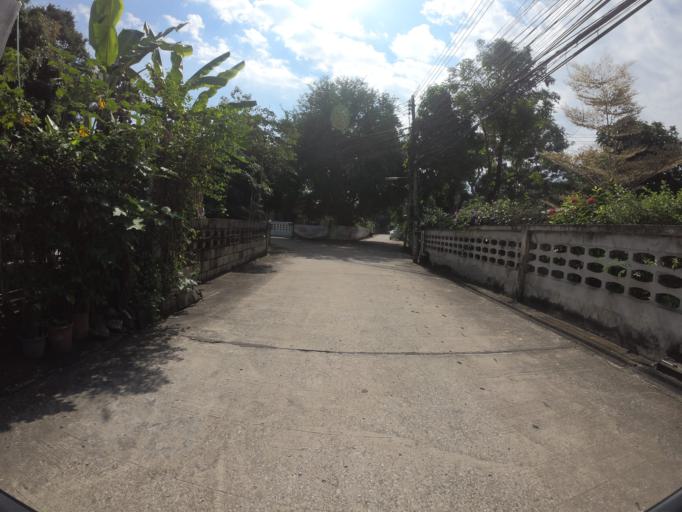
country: TH
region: Chiang Mai
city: Chiang Mai
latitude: 18.7898
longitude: 98.9589
